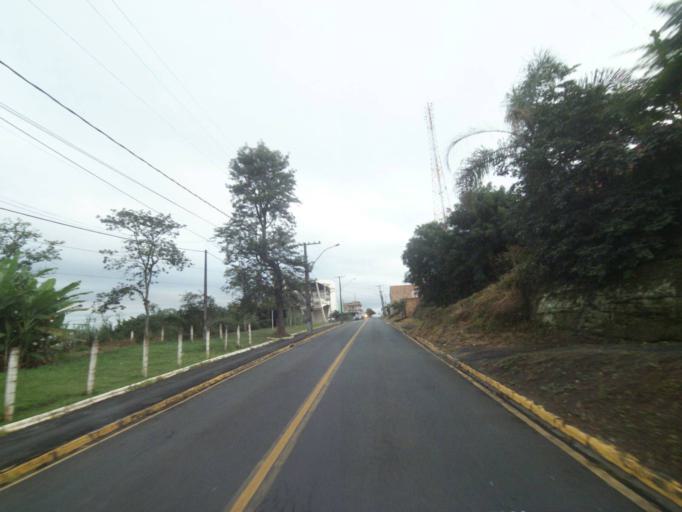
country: BR
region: Parana
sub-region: Telemaco Borba
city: Telemaco Borba
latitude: -24.3177
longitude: -50.6171
